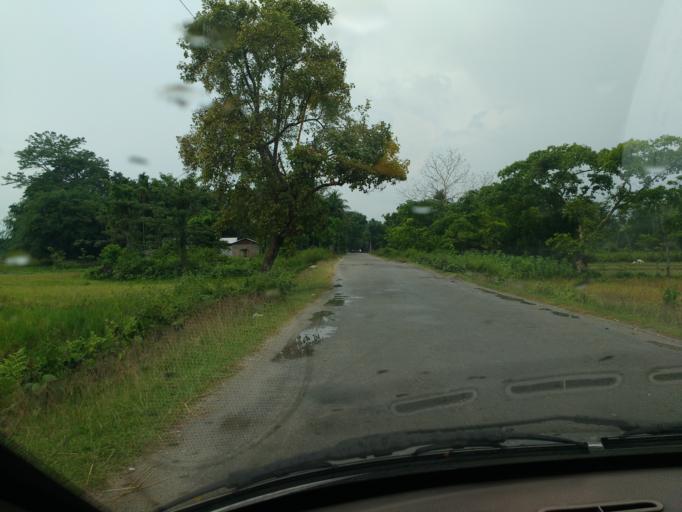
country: IN
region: Assam
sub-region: Udalguri
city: Udalguri
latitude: 26.7269
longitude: 92.2118
